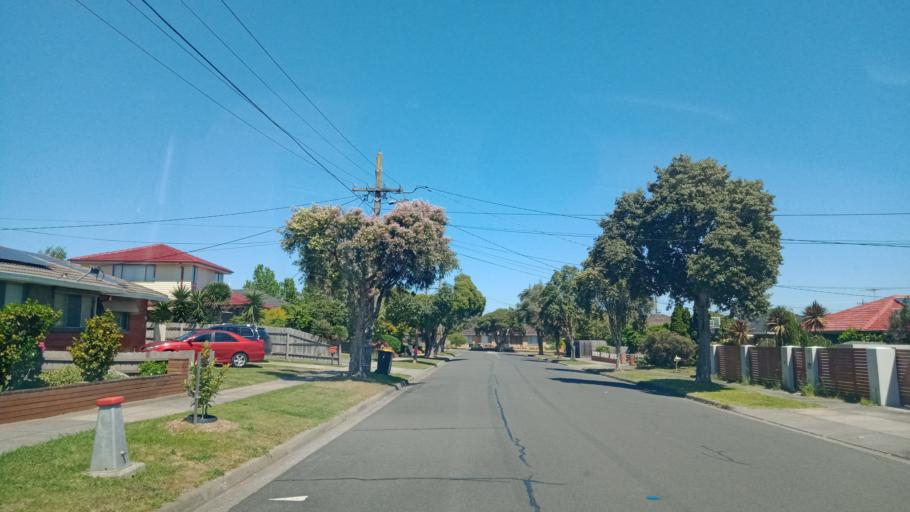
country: AU
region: Victoria
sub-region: Greater Dandenong
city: Springvale
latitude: -37.9275
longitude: 145.1612
